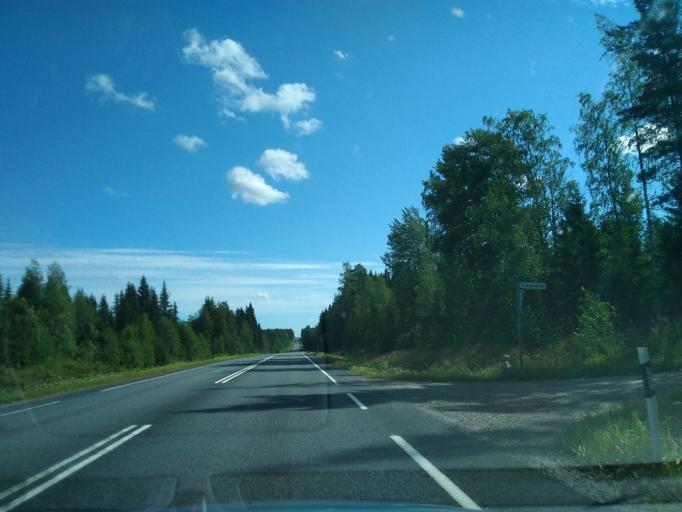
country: FI
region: Haeme
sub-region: Haemeenlinna
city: Renko
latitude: 60.8362
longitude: 24.0780
